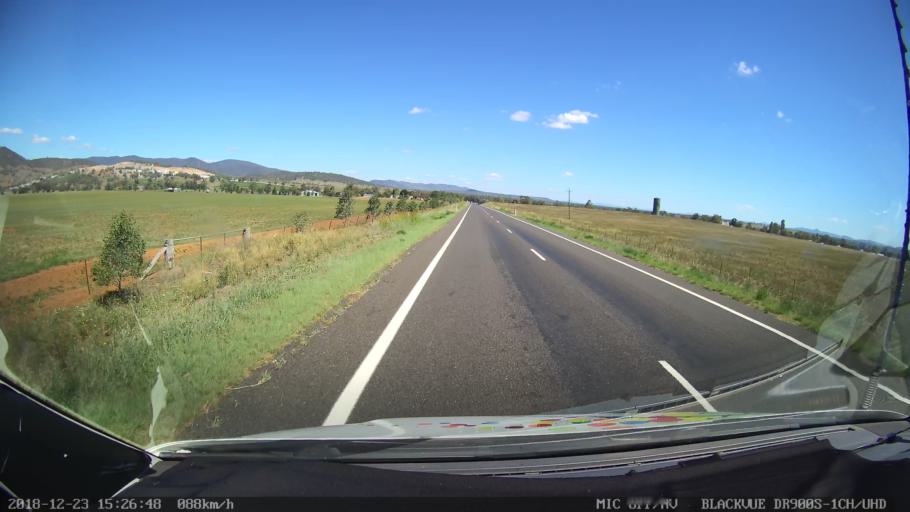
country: AU
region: New South Wales
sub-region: Tamworth Municipality
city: East Tamworth
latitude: -30.9212
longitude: 150.8411
